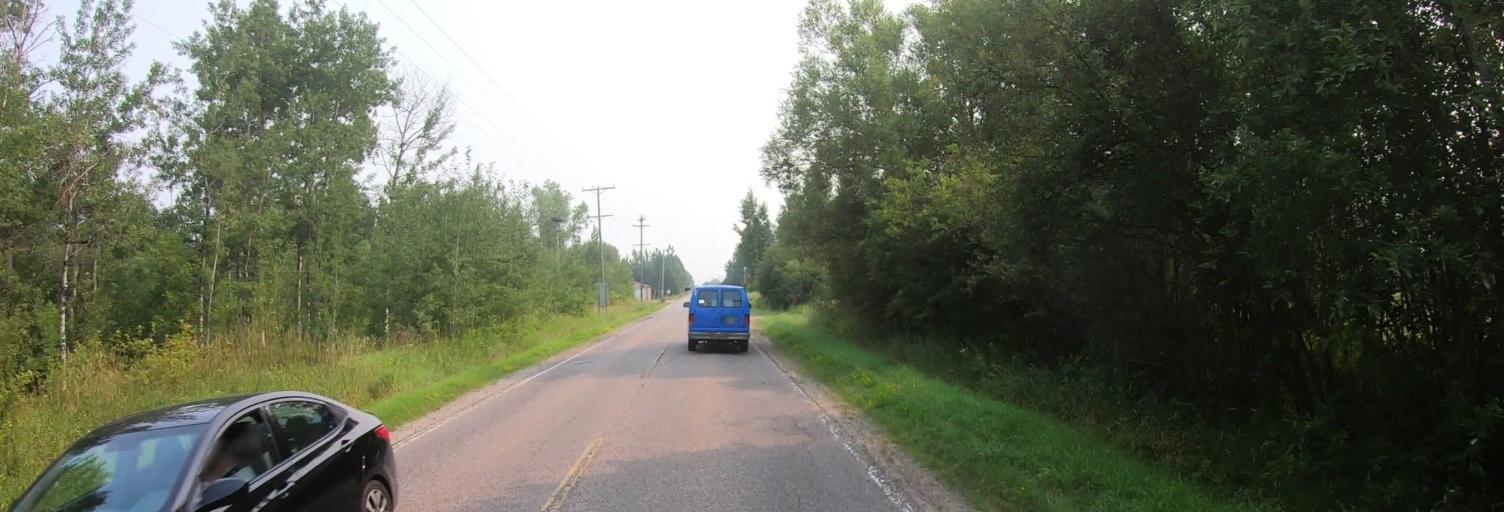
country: US
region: Michigan
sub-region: Chippewa County
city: Sault Ste. Marie
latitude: 46.4643
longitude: -84.3013
